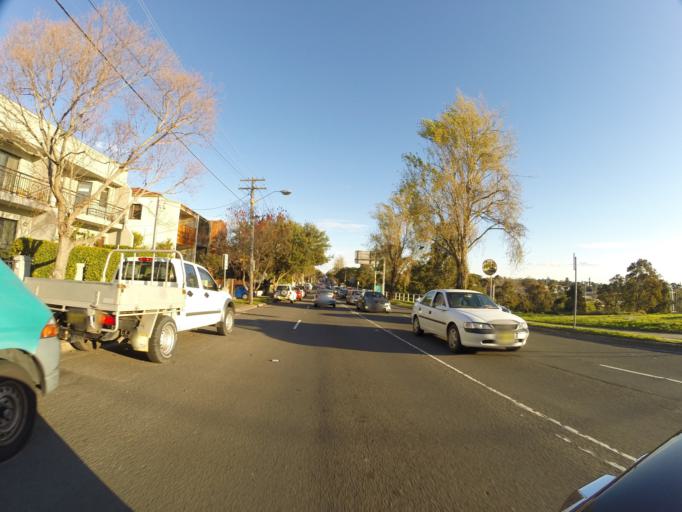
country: AU
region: New South Wales
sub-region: Waverley
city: Bondi Junction
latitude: -33.9019
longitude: 151.2533
